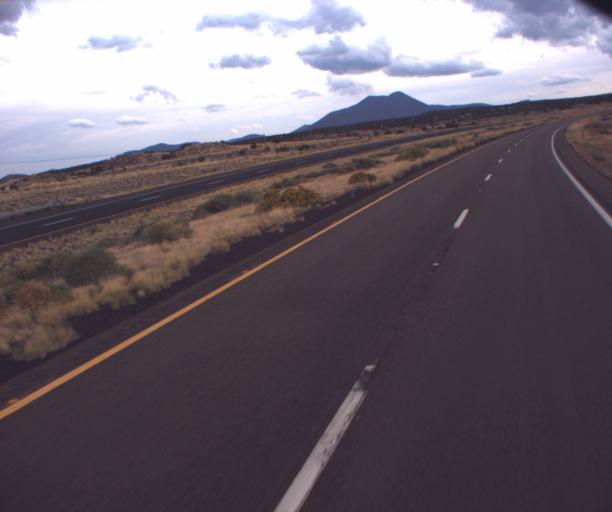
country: US
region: Arizona
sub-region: Coconino County
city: Flagstaff
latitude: 35.5172
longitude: -111.5443
